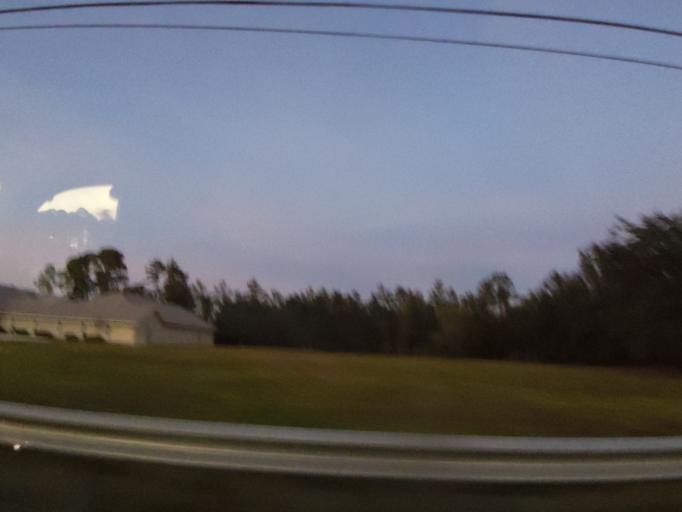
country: US
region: Florida
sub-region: Saint Johns County
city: Saint Augustine South
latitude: 29.8300
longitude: -81.3552
